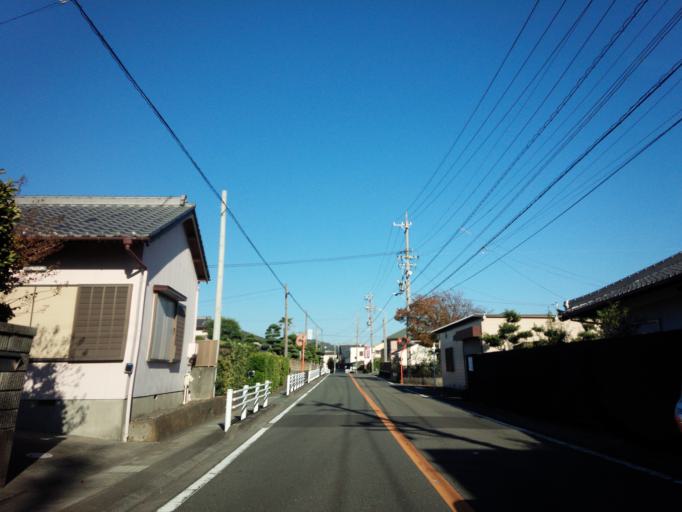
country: JP
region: Shizuoka
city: Shizuoka-shi
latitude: 34.9453
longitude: 138.4143
